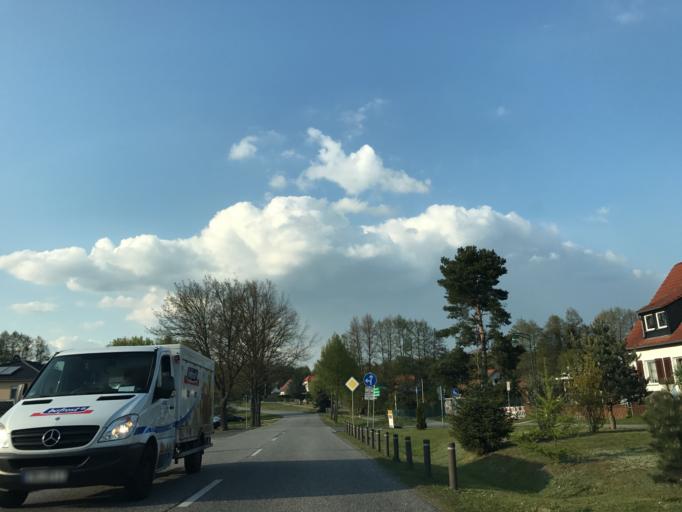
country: DE
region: Brandenburg
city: Wustermark
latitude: 52.5215
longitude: 12.9813
